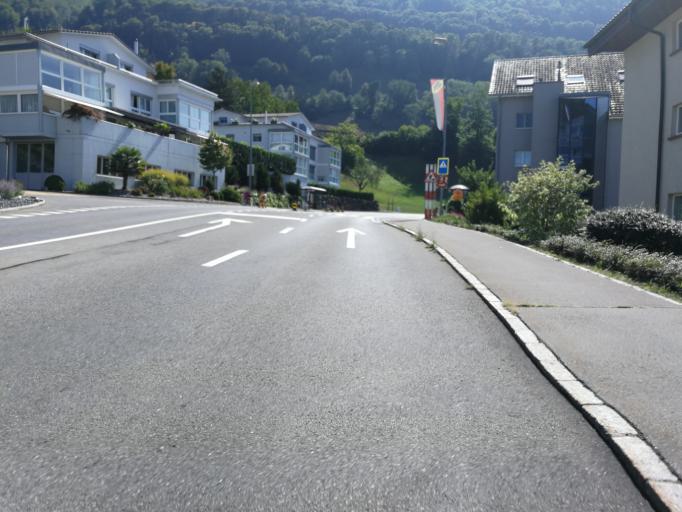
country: CH
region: Lucerne
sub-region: Lucerne-Land District
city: Weggis
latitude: 47.0566
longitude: 8.4304
